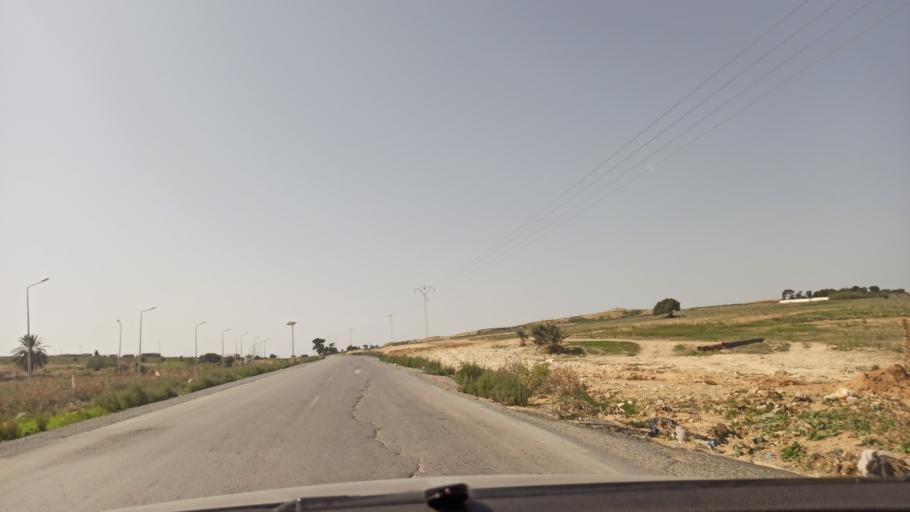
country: TN
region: Manouba
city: Manouba
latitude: 36.7406
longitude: 10.0874
